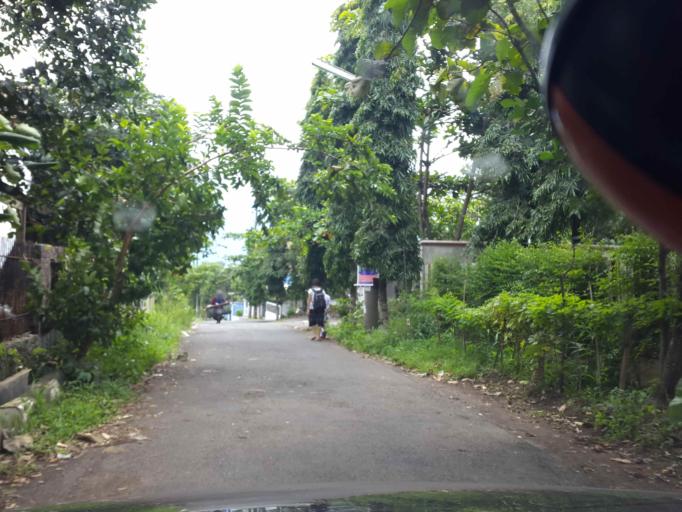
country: ID
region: Central Java
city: Salatiga
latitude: -7.3060
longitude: 110.4882
